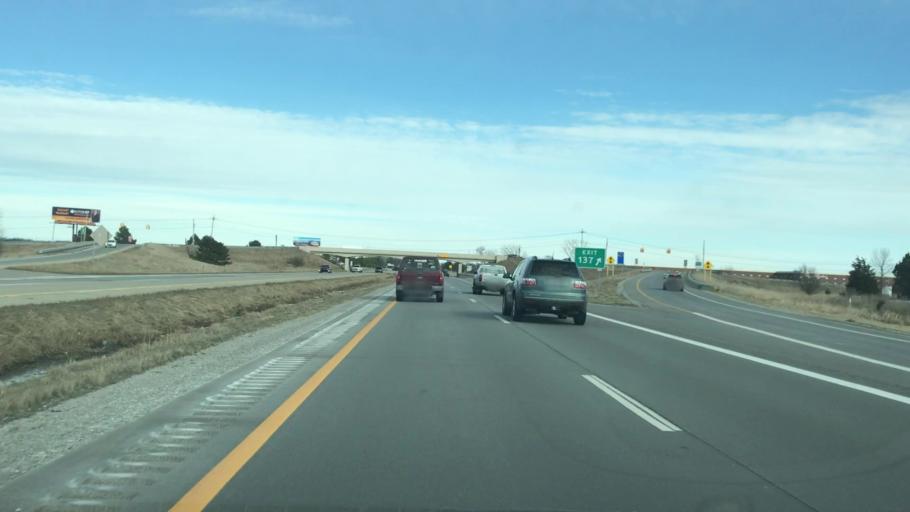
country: US
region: Michigan
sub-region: Bay County
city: Auburn
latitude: 43.5960
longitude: -83.9955
